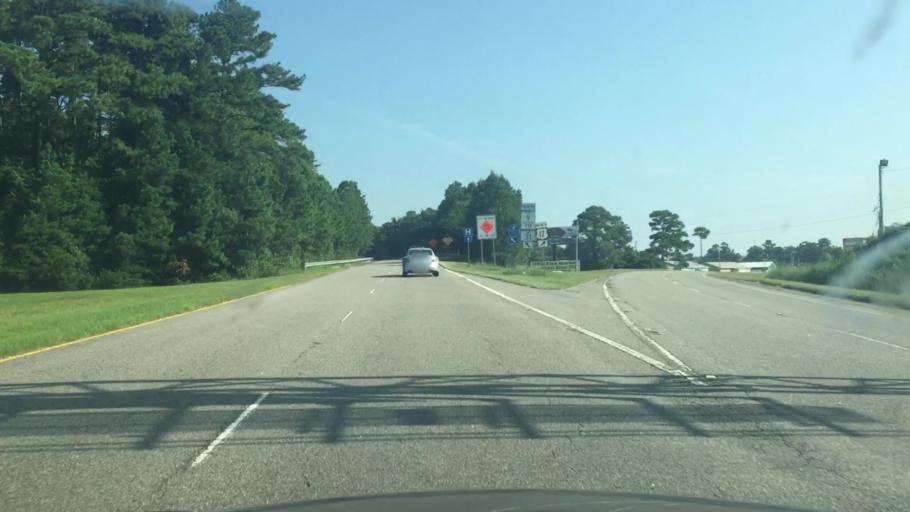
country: US
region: South Carolina
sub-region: Horry County
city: Little River
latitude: 33.8604
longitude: -78.6567
